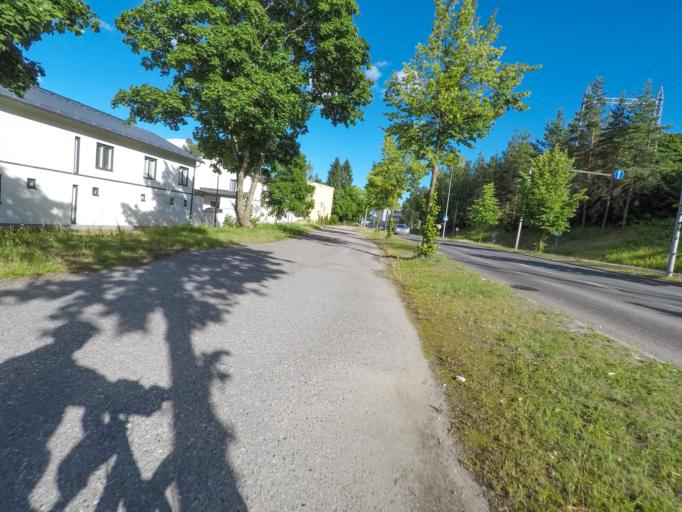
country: FI
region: South Karelia
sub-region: Lappeenranta
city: Lappeenranta
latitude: 61.0635
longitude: 28.1752
